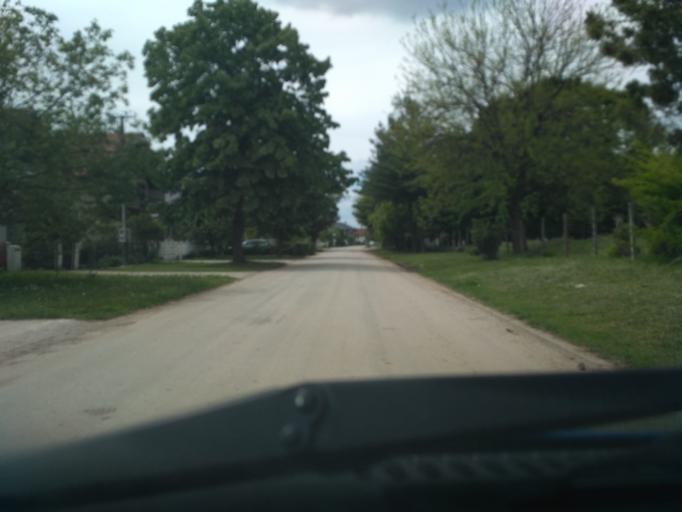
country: RS
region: Central Serbia
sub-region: Pomoravski Okrug
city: Svilajnac
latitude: 44.2262
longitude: 21.2074
